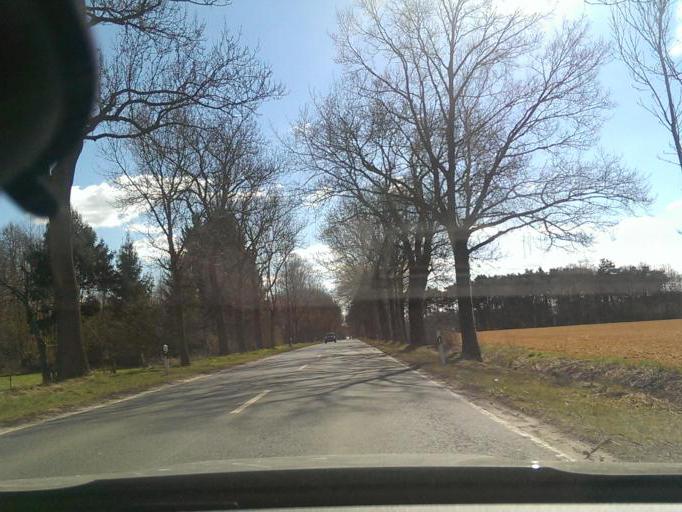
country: DE
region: Lower Saxony
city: Elze
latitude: 52.5738
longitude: 9.7272
